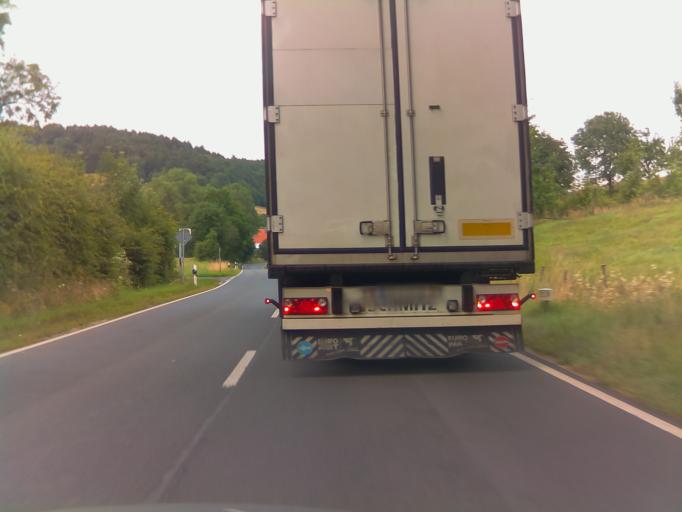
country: DE
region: Hesse
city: Grebenau
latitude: 50.7779
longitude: 9.4666
